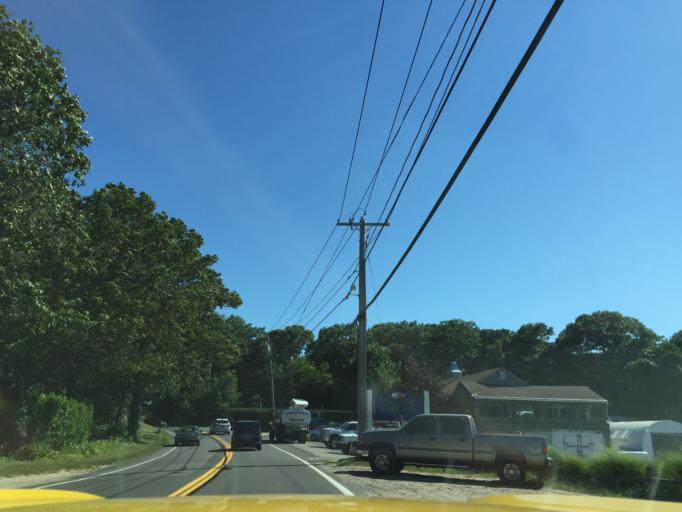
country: US
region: New York
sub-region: Suffolk County
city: North Sea
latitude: 40.9537
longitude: -72.3938
